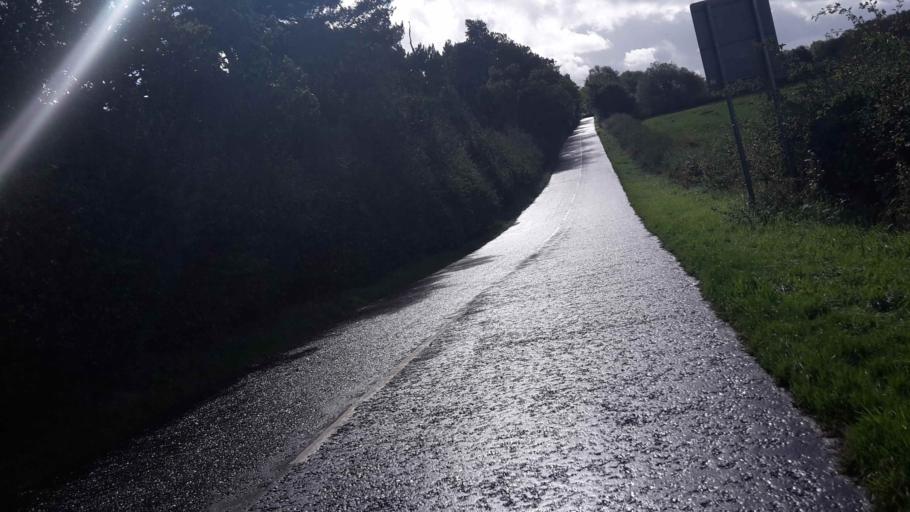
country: GB
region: Scotland
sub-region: South Lanarkshire
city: Carluke
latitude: 55.7278
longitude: -3.8544
